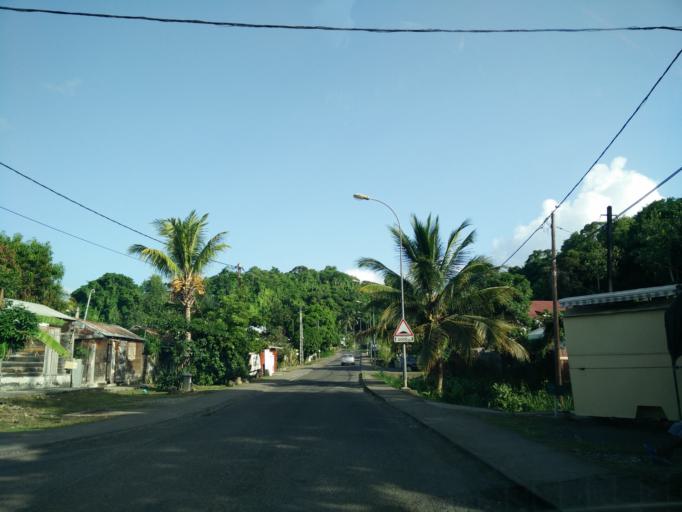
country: GP
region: Guadeloupe
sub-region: Guadeloupe
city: Les Abymes
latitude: 16.2513
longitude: -61.5131
